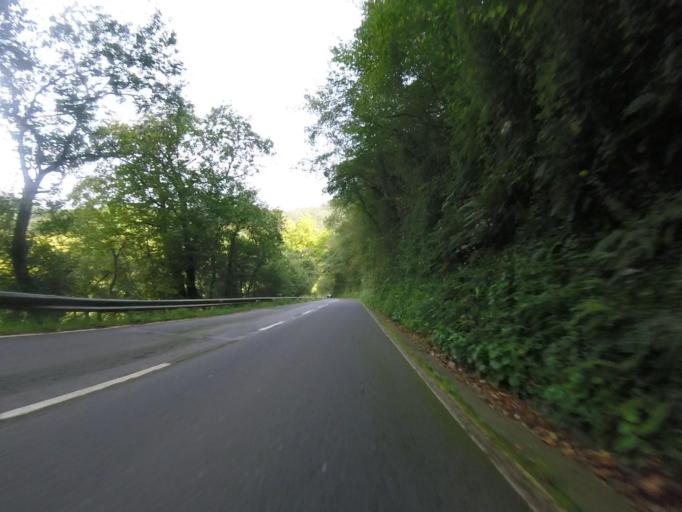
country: ES
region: Navarre
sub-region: Provincia de Navarra
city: Arano
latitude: 43.2197
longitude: -1.9088
